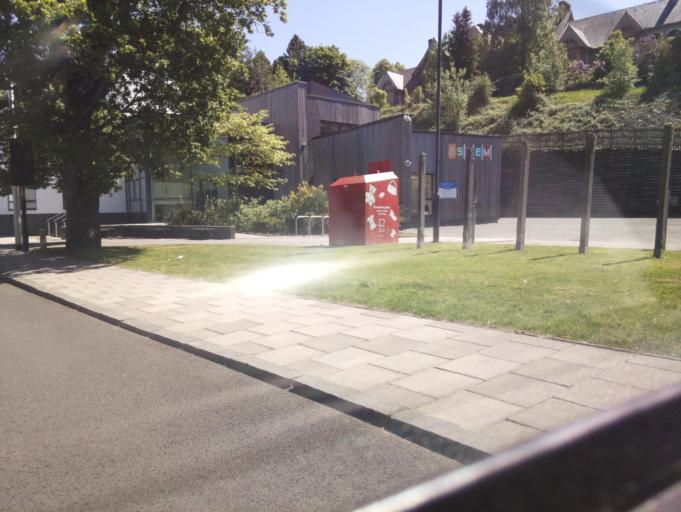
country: GB
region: Scotland
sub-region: The Scottish Borders
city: Hawick
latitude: 55.4211
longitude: -2.7975
